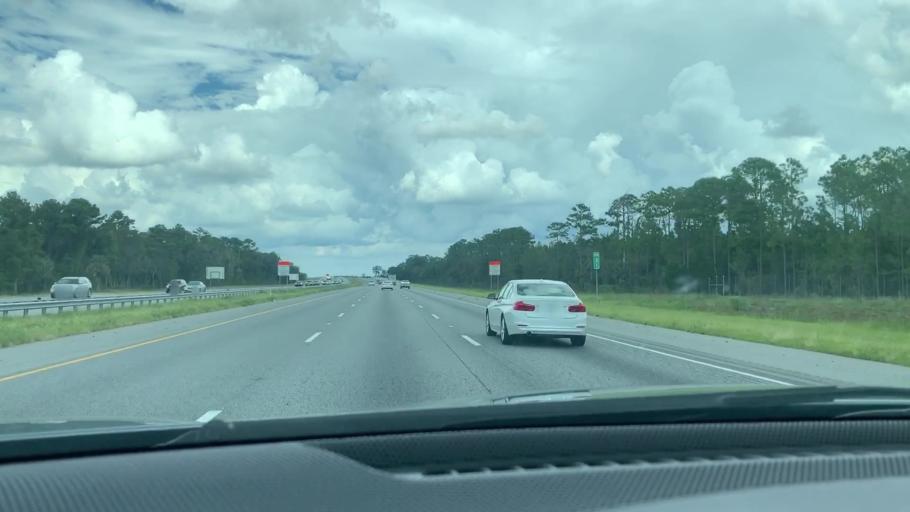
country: US
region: Georgia
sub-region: Glynn County
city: Dock Junction
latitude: 31.1591
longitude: -81.5590
